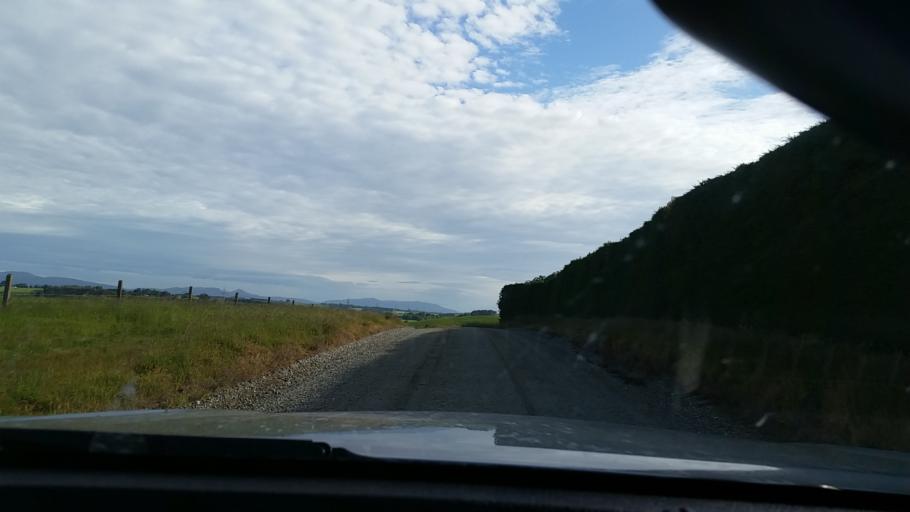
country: NZ
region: Southland
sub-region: Gore District
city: Gore
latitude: -46.2679
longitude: 168.7182
